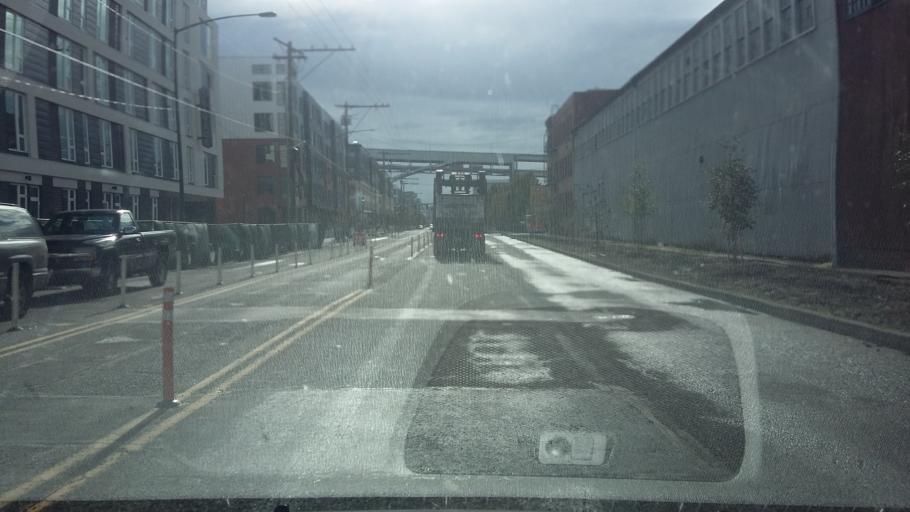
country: US
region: Oregon
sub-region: Multnomah County
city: Portland
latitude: 45.5393
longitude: -122.6908
